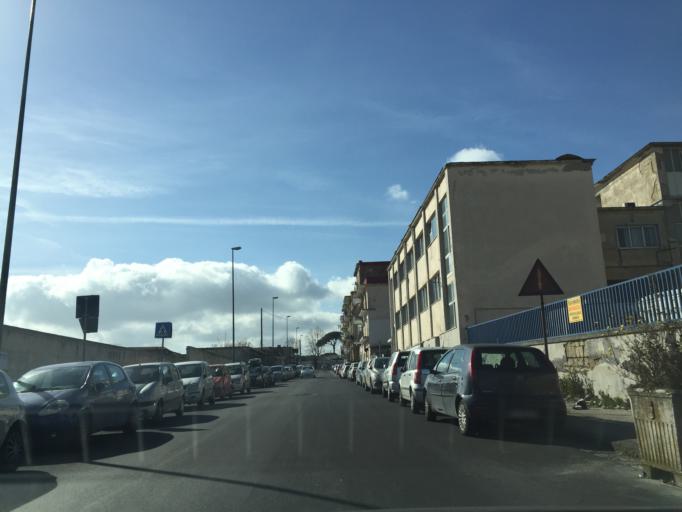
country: IT
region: Campania
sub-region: Provincia di Napoli
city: Casavatore
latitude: 40.8697
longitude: 14.2874
